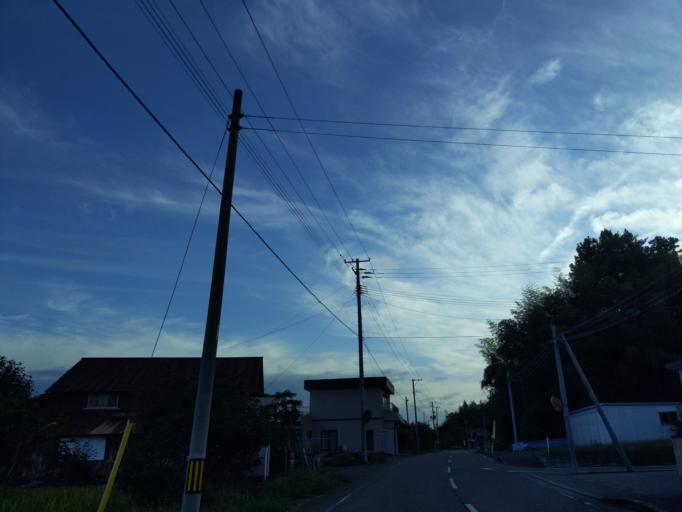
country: JP
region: Niigata
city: Kashiwazaki
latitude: 37.4357
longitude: 138.6246
